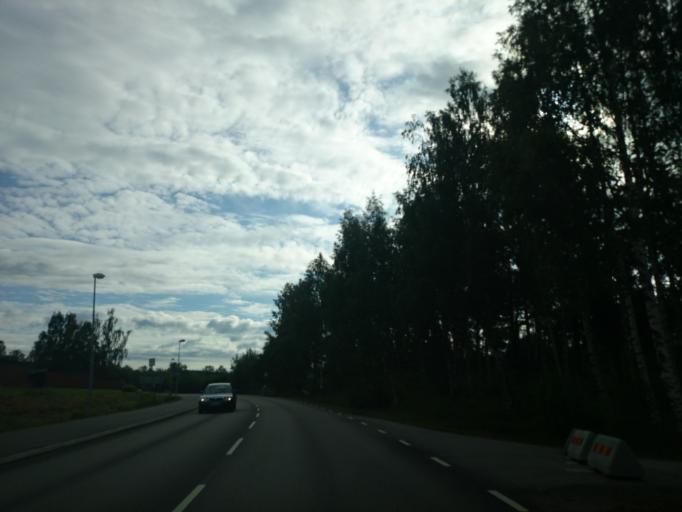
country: SE
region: Vaesternorrland
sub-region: Sundsvalls Kommun
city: Johannedal
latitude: 62.4322
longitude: 17.3828
